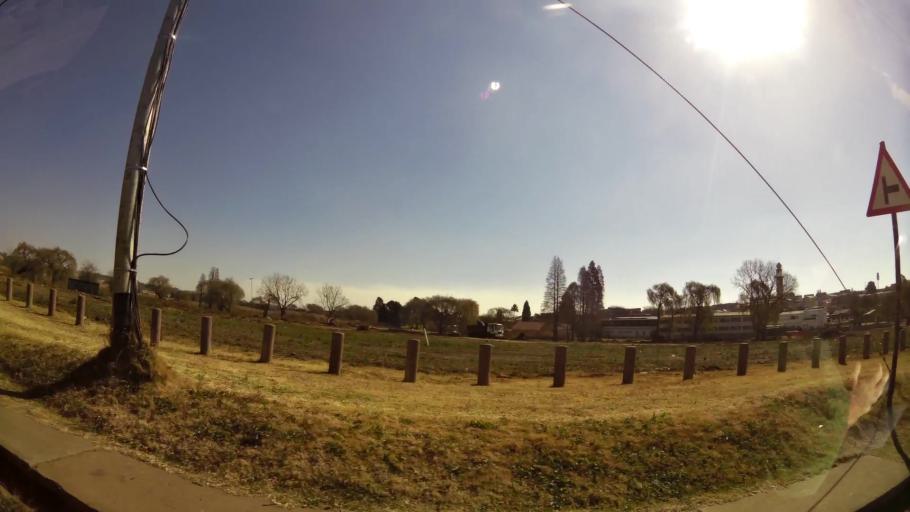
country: ZA
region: Gauteng
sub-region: City of Johannesburg Metropolitan Municipality
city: Johannesburg
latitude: -26.1923
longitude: 27.9570
